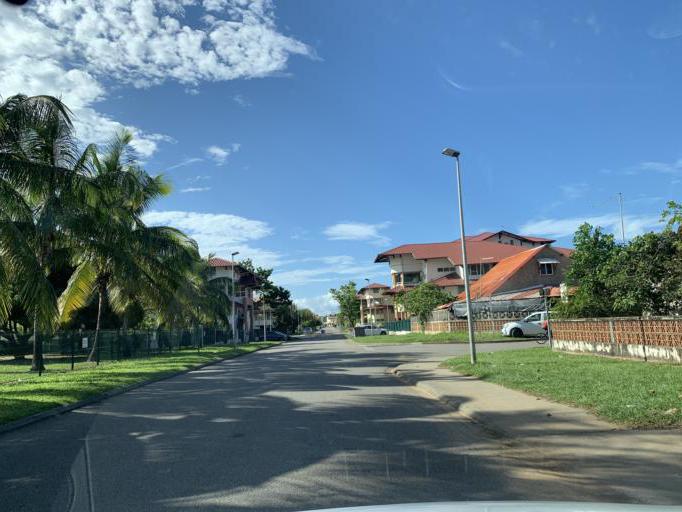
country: GF
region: Guyane
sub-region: Guyane
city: Kourou
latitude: 5.1735
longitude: -52.6476
